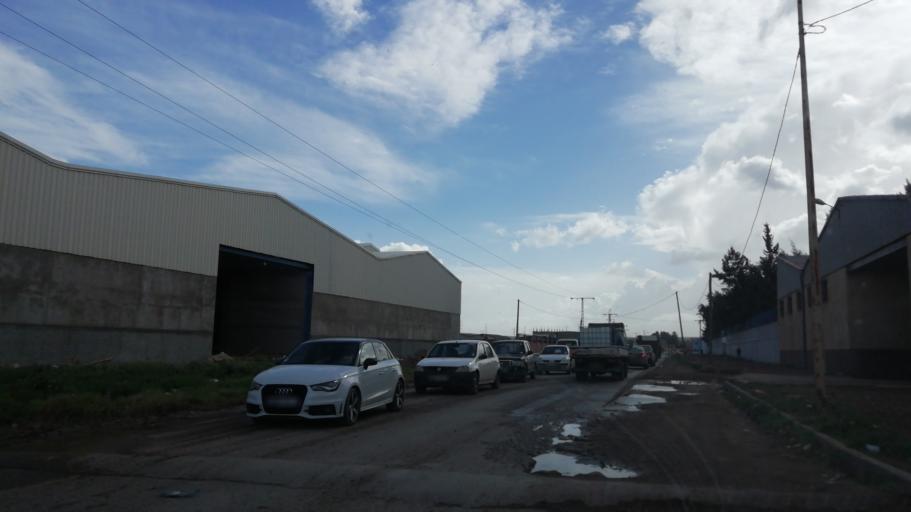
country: DZ
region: Oran
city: Sidi ech Chahmi
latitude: 35.6422
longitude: -0.5544
